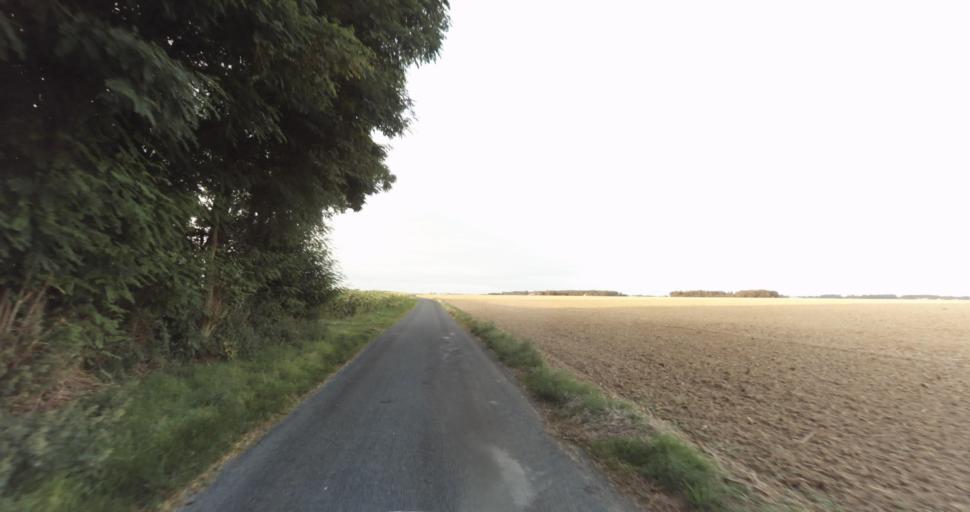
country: FR
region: Haute-Normandie
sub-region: Departement de l'Eure
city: La Madeleine-de-Nonancourt
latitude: 48.8842
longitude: 1.2072
